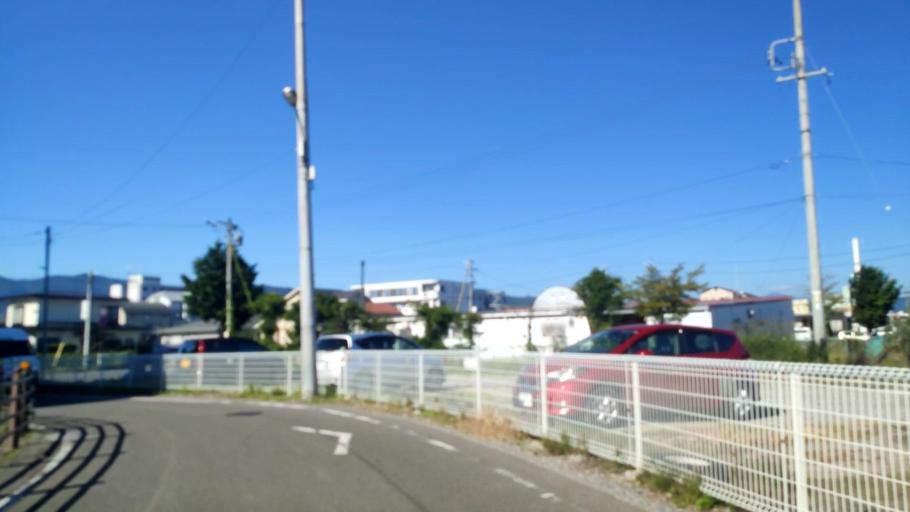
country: JP
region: Nagano
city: Suwa
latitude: 36.0401
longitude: 138.1120
